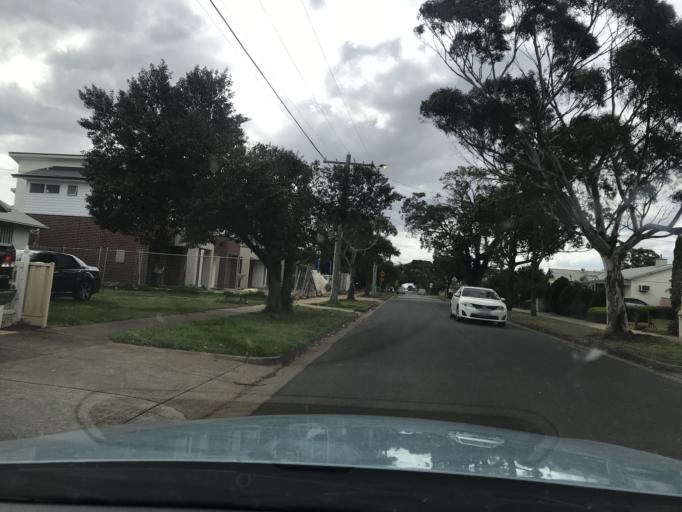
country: AU
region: Victoria
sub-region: Hobsons Bay
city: Laverton
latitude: -37.8544
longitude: 144.7708
